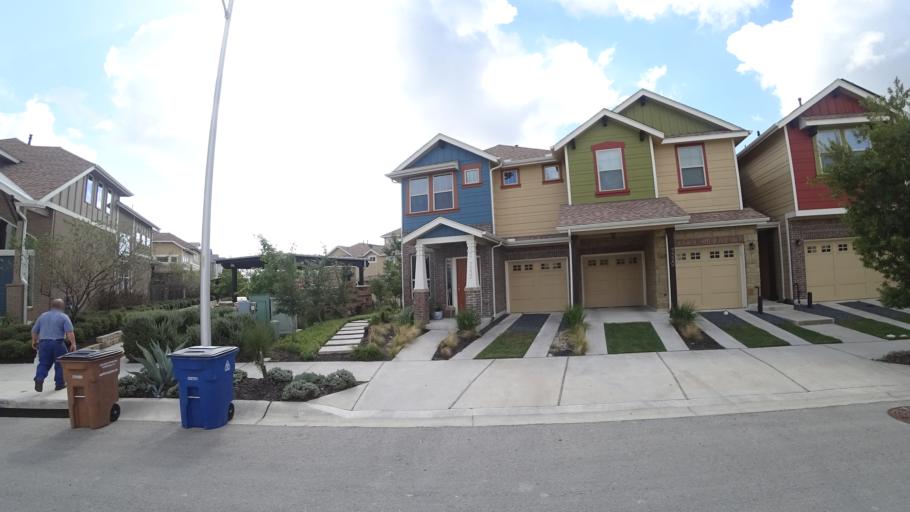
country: US
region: Texas
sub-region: Travis County
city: Austin
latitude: 30.3425
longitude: -97.7197
